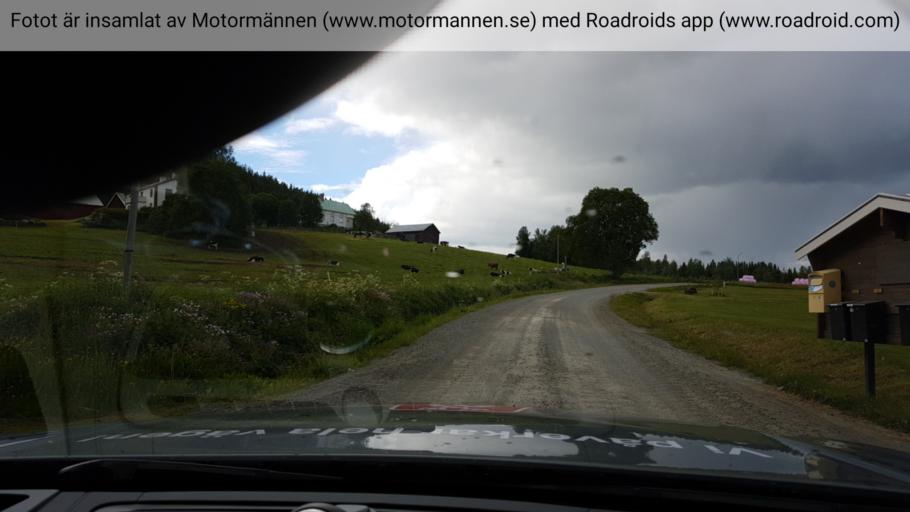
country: SE
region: Jaemtland
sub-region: Bergs Kommun
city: Hoverberg
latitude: 62.9386
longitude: 14.2733
